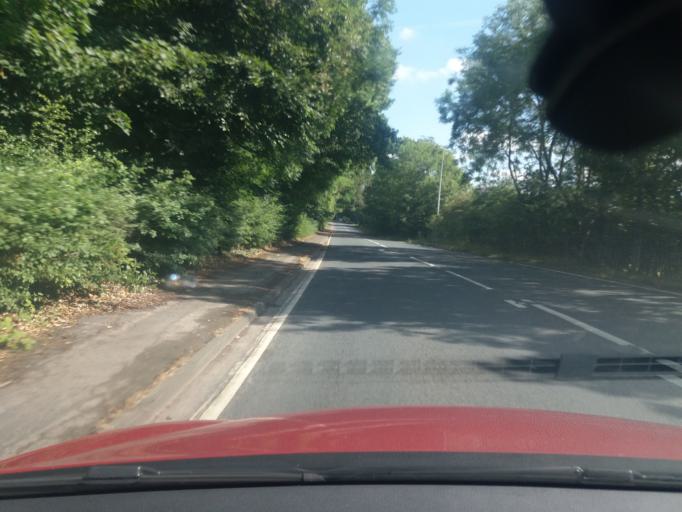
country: GB
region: England
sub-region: Lancashire
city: Adlington
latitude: 53.6261
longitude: -2.6192
